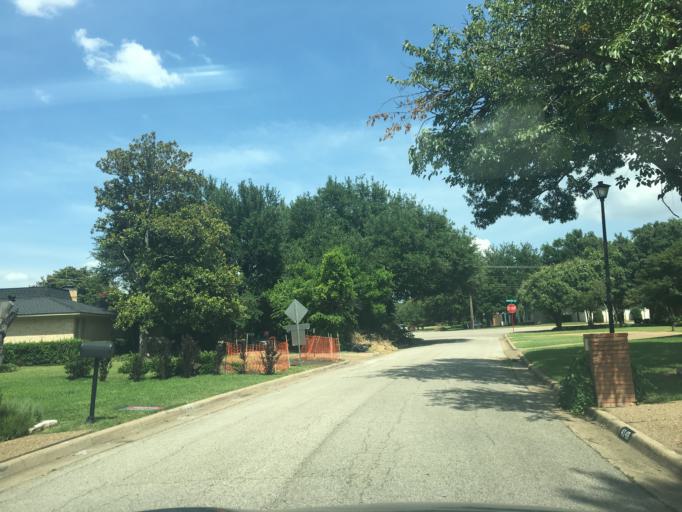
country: US
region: Texas
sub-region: Dallas County
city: Addison
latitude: 32.9122
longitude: -96.8395
